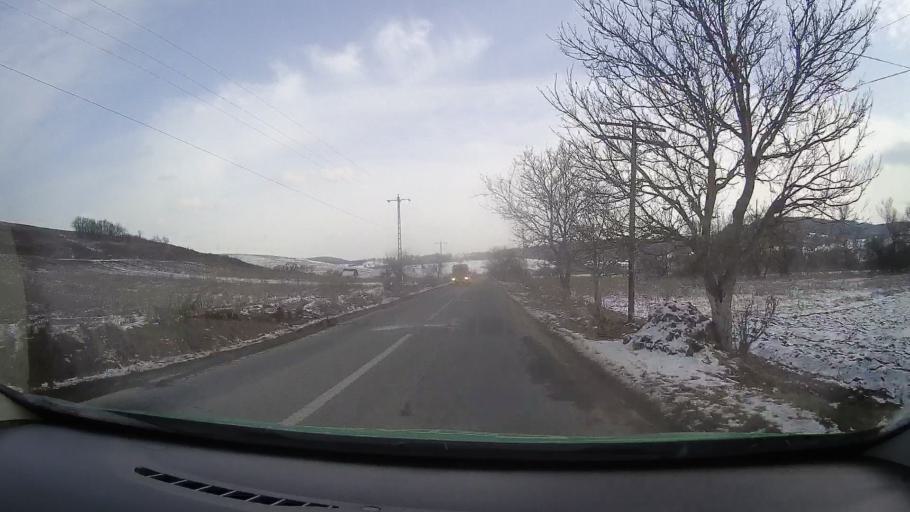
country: RO
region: Mures
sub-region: Comuna Apold
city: Saes
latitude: 46.1449
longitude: 24.7788
